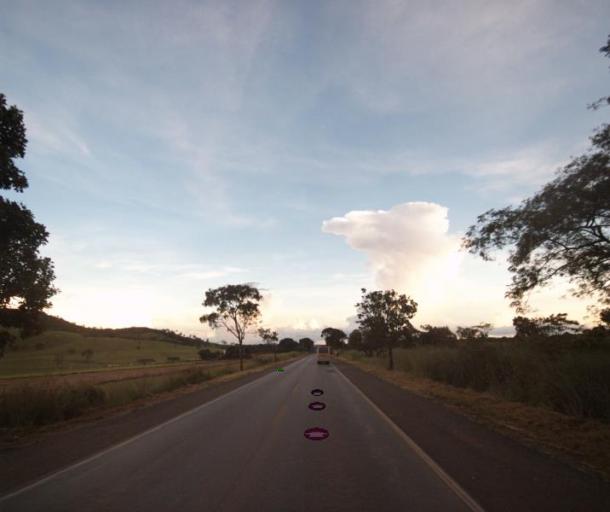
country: BR
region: Goias
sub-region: Uruacu
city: Uruacu
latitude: -14.3991
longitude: -49.1576
